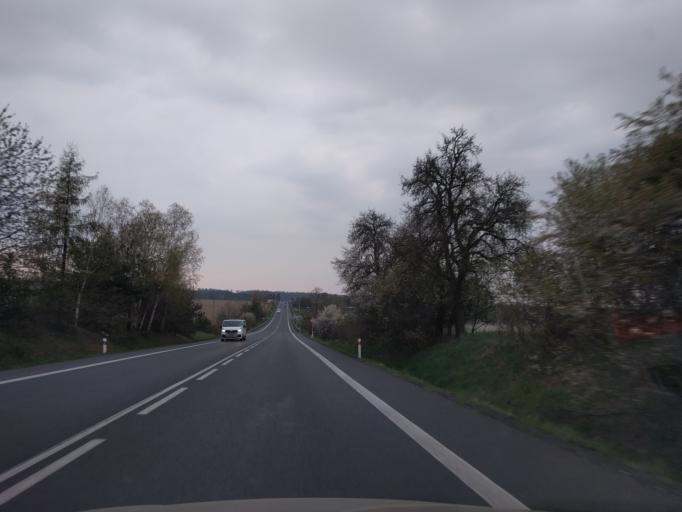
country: CZ
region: Central Bohemia
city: Kostelec nad Cernymi Lesy
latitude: 49.9923
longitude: 14.8236
